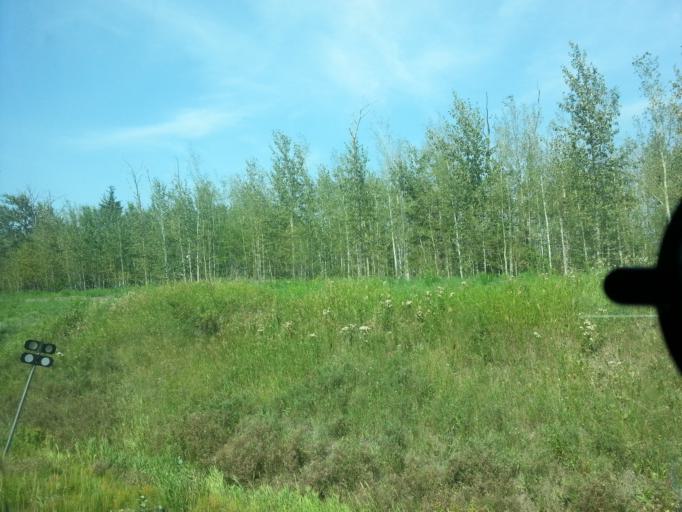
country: CA
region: Alberta
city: Drayton Valley
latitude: 53.5940
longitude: -115.0065
